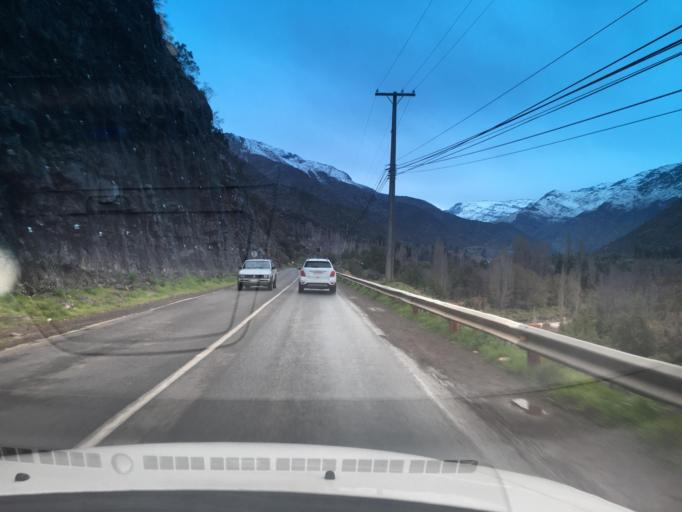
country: CL
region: Santiago Metropolitan
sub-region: Provincia de Cordillera
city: Puente Alto
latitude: -33.6737
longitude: -70.3448
